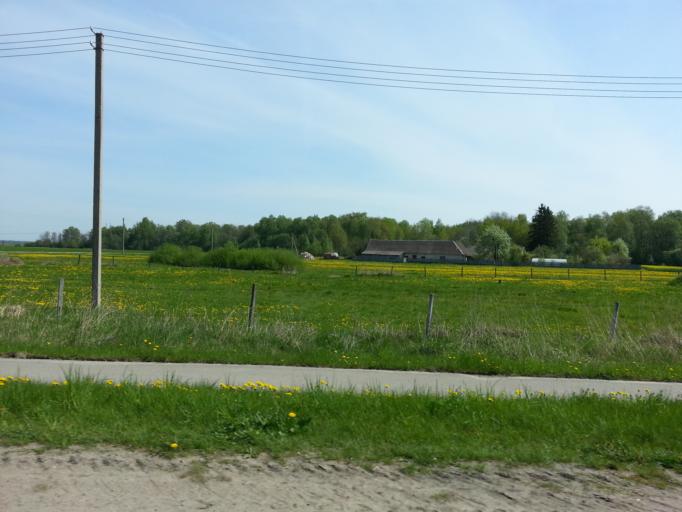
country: LT
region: Panevezys
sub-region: Panevezys City
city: Panevezys
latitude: 55.7736
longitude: 24.2937
